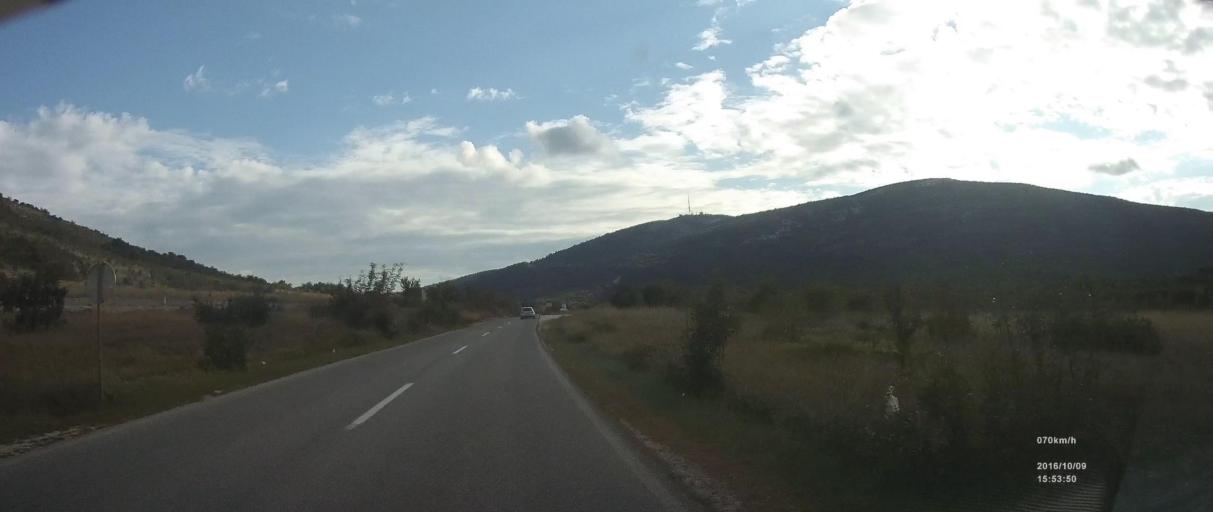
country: HR
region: Splitsko-Dalmatinska
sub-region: Grad Trogir
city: Trogir
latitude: 43.6014
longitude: 16.2248
